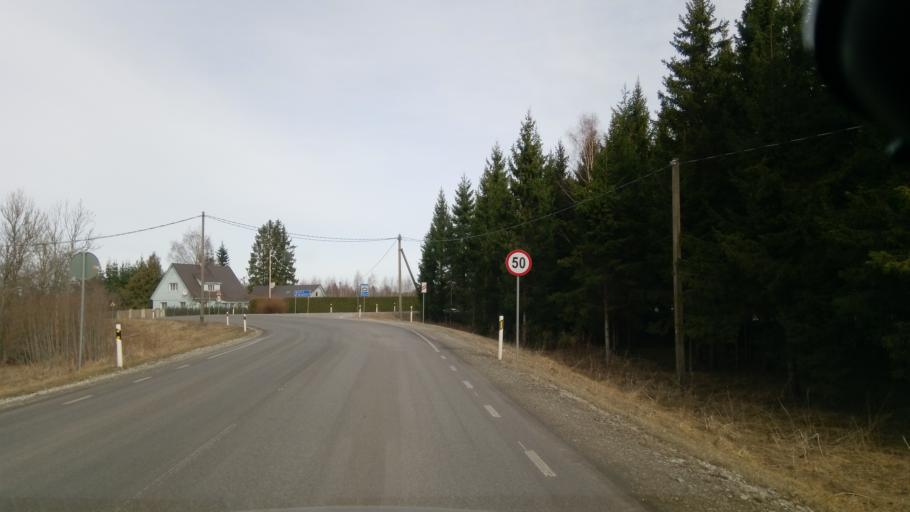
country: EE
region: Raplamaa
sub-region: Rapla vald
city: Rapla
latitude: 59.0175
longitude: 24.8379
